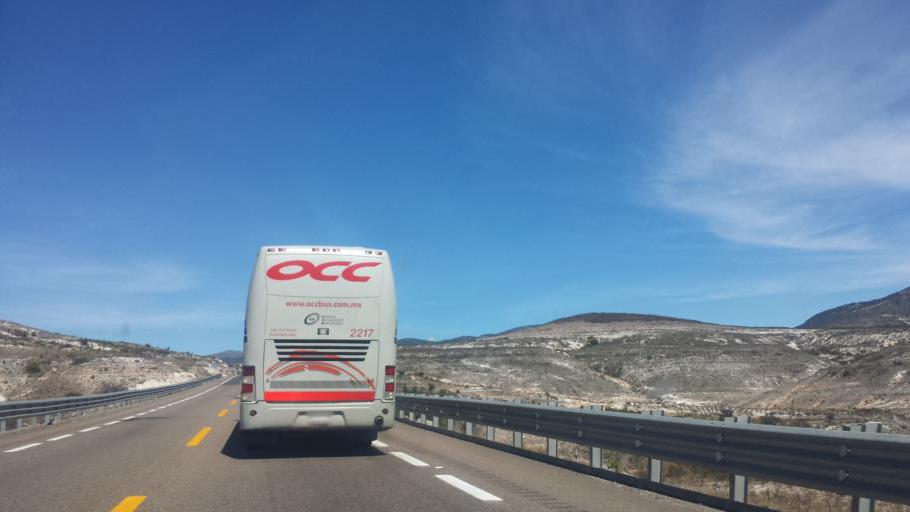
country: MX
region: Oaxaca
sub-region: Villa Tejupam de la Union
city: Villa Tejupam de la Union
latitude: 17.9018
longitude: -97.3670
